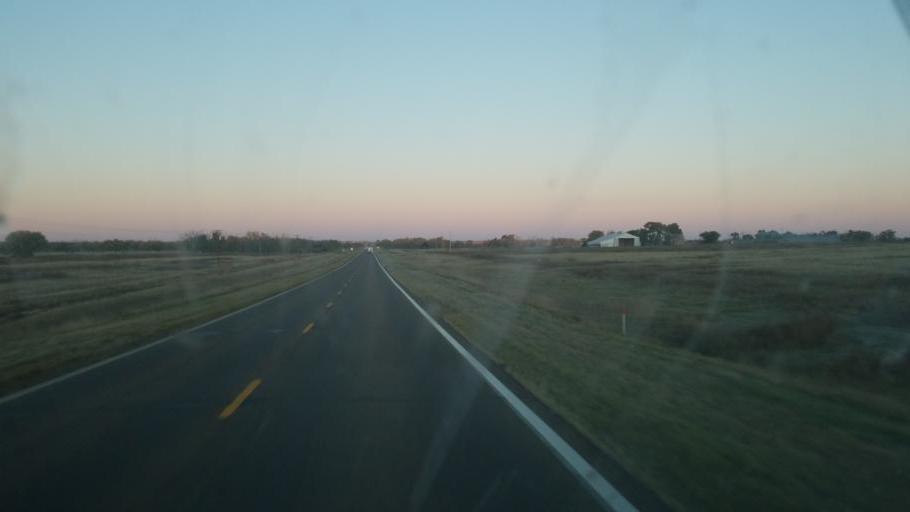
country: US
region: Kansas
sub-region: Wallace County
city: Sharon Springs
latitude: 38.9023
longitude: -101.6802
